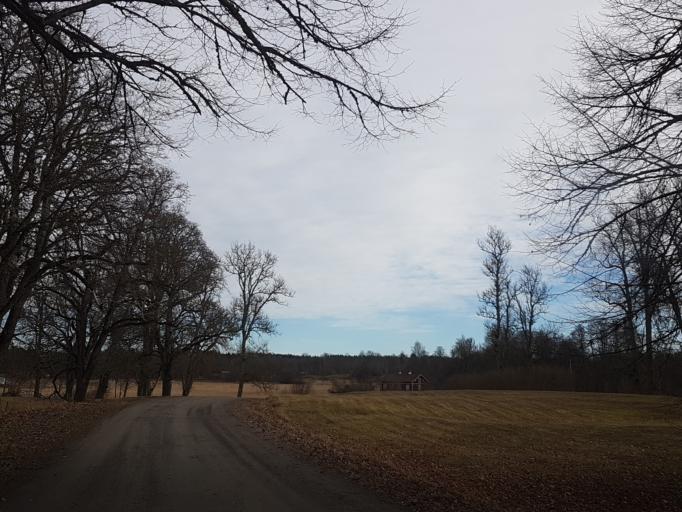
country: SE
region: Stockholm
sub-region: Norrtalje Kommun
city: Norrtalje
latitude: 59.6822
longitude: 18.6734
